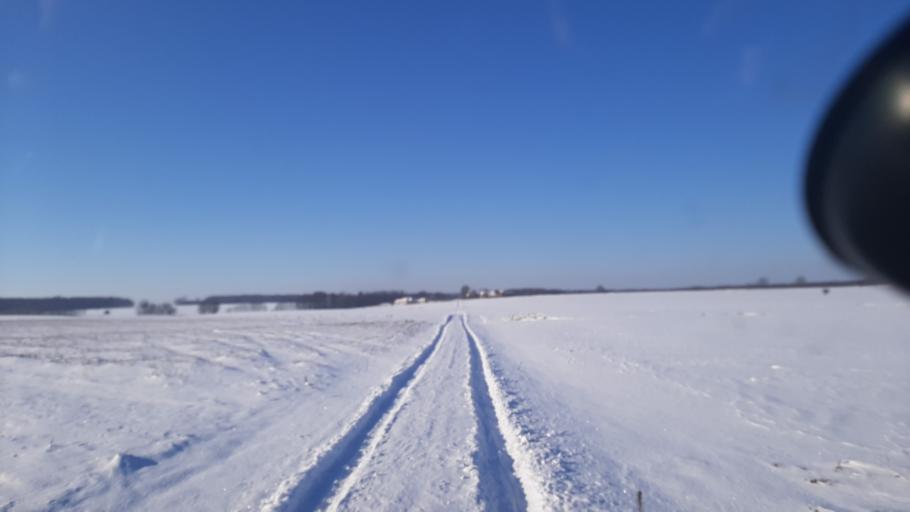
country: PL
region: Lublin Voivodeship
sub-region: Powiat lubelski
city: Jastkow
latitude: 51.3804
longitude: 22.4295
